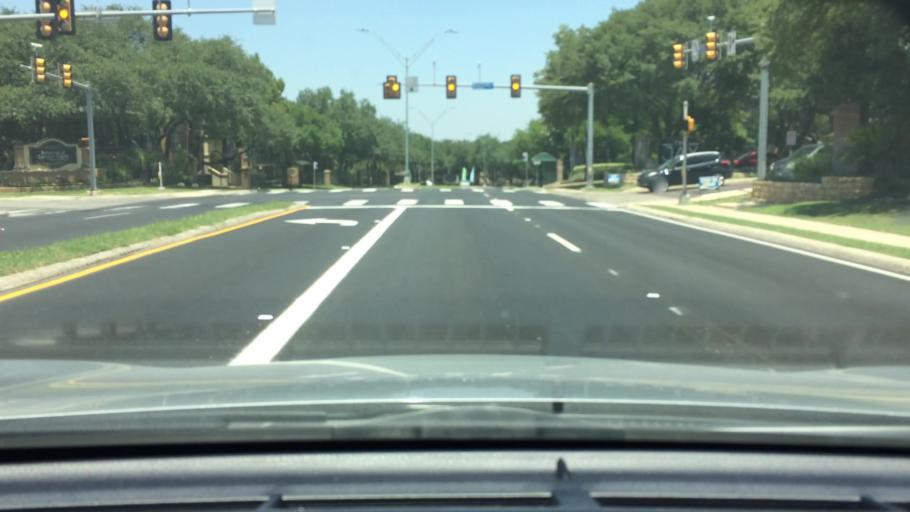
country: US
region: Texas
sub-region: Bexar County
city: Shavano Park
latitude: 29.5540
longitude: -98.5732
